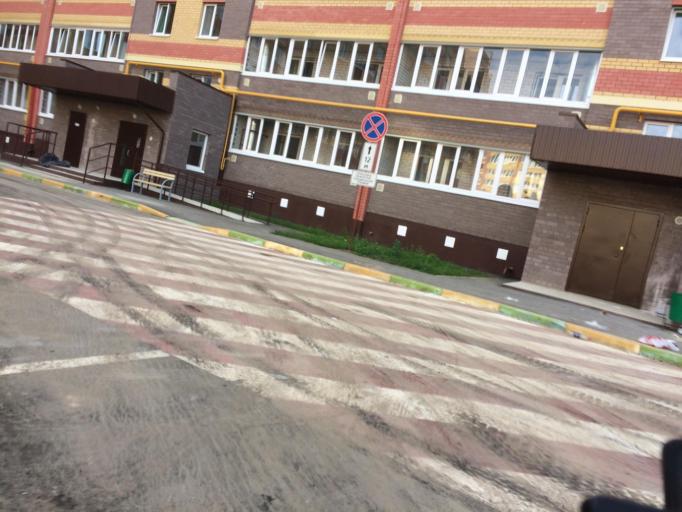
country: RU
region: Mariy-El
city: Medvedevo
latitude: 56.6366
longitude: 47.8222
